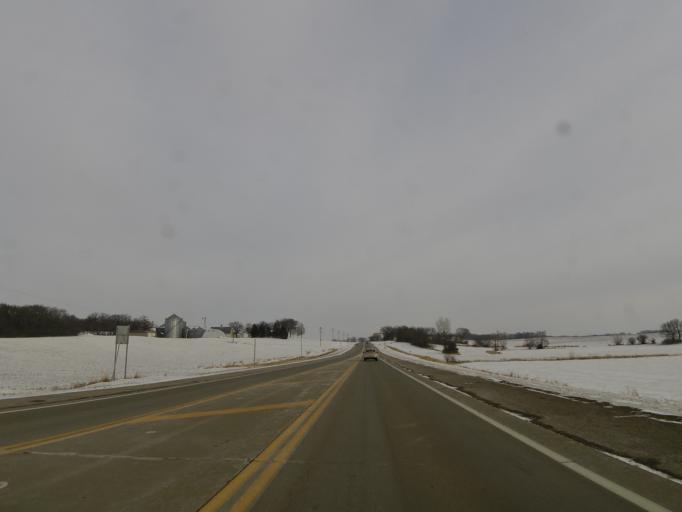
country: US
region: Minnesota
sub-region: McLeod County
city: Hutchinson
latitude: 44.8926
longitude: -94.2409
